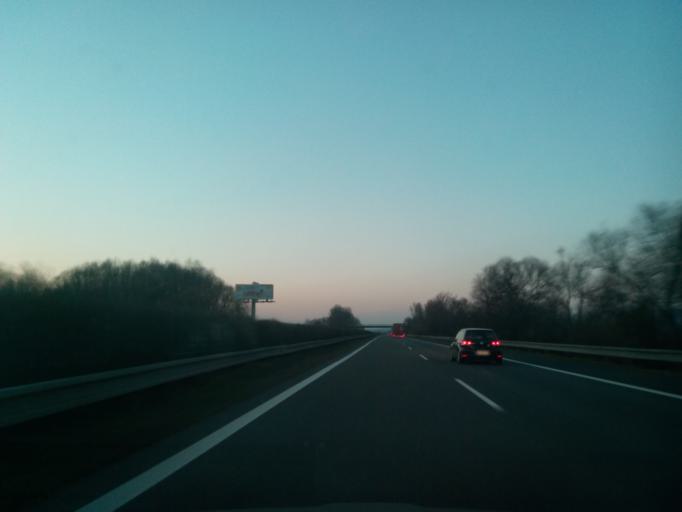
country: SK
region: Kosicky
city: Kosice
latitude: 48.7959
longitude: 21.3123
